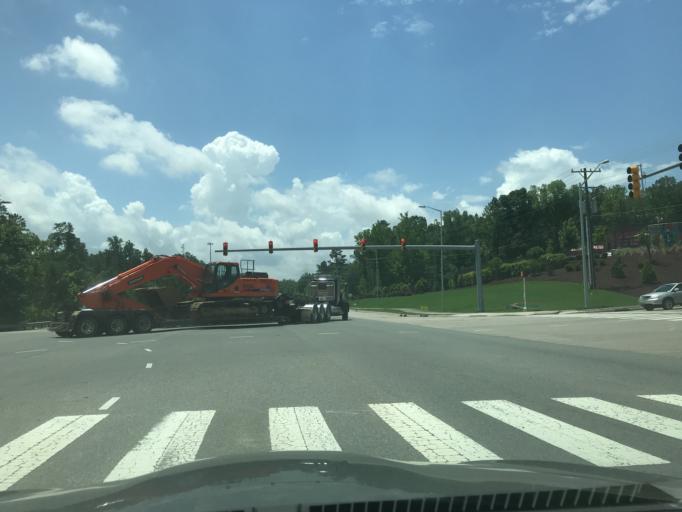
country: US
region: North Carolina
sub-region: Wake County
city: Morrisville
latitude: 35.8611
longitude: -78.8938
